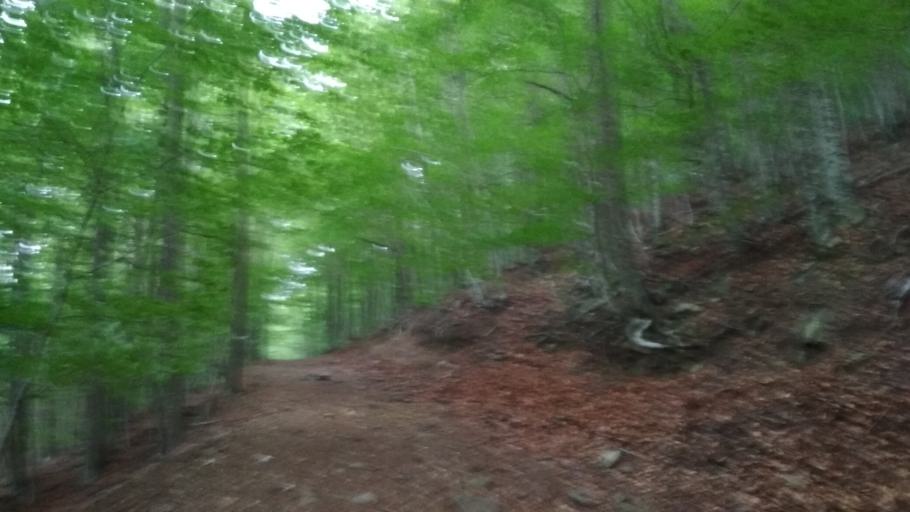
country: ES
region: Catalonia
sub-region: Provincia de Barcelona
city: Fogars de Montclus
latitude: 41.7774
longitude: 2.4500
